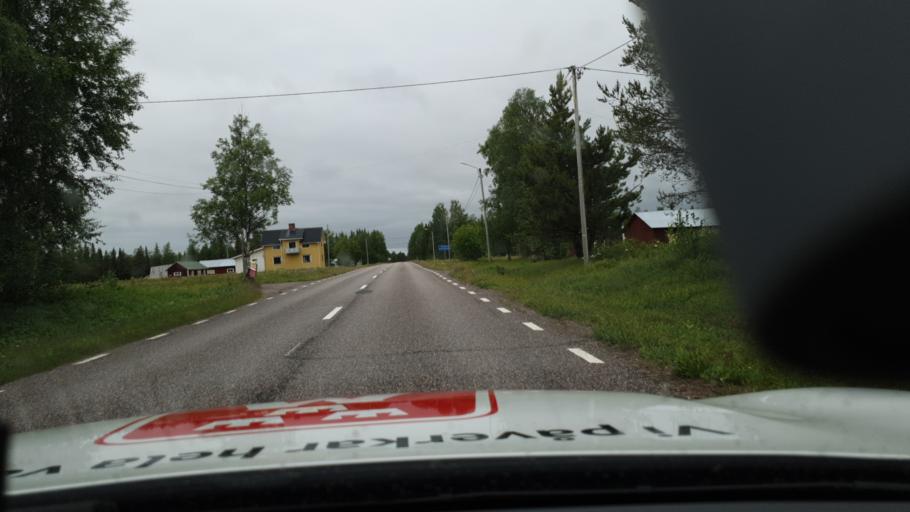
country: SE
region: Norrbotten
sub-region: Pajala Kommun
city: Pajala
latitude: 67.1901
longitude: 23.4740
